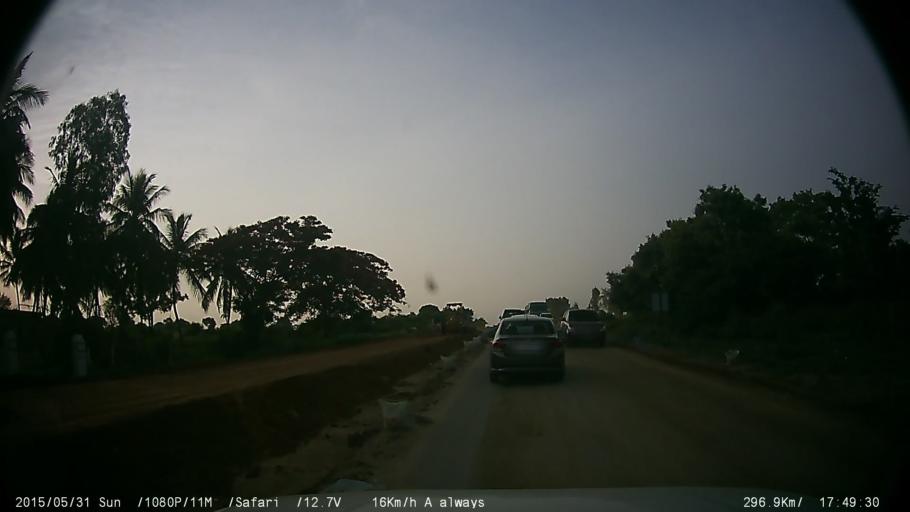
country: IN
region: Karnataka
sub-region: Mysore
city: Nanjangud
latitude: 11.9712
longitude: 76.6703
